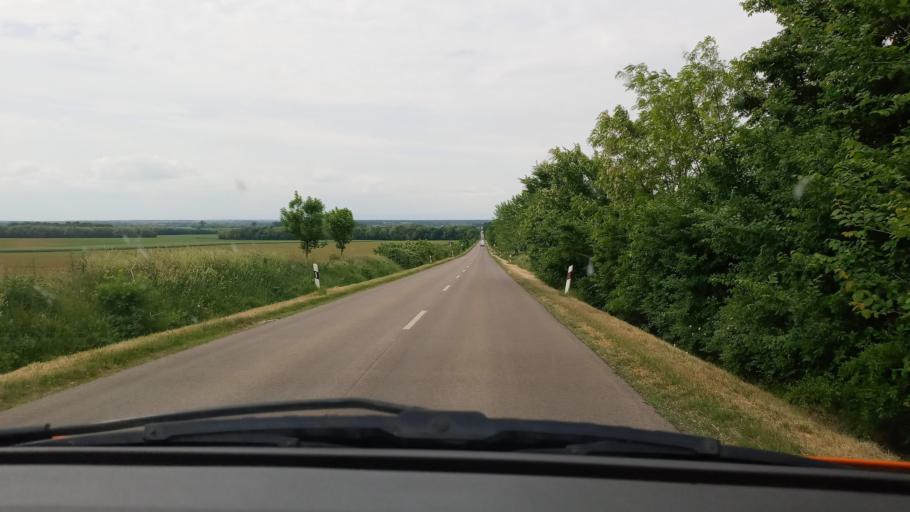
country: HU
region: Baranya
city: Vajszlo
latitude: 45.9346
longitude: 18.0696
